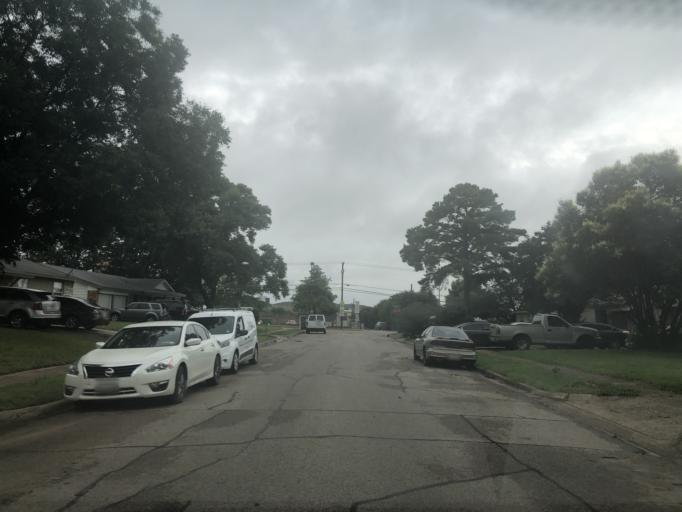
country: US
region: Texas
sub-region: Dallas County
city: Irving
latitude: 32.7946
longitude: -96.9488
